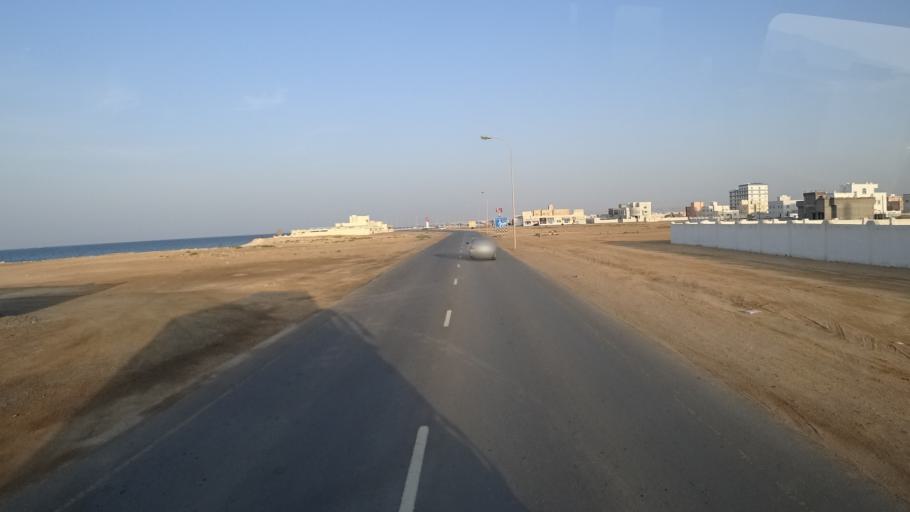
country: OM
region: Ash Sharqiyah
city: Sur
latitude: 22.6049
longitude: 59.4786
